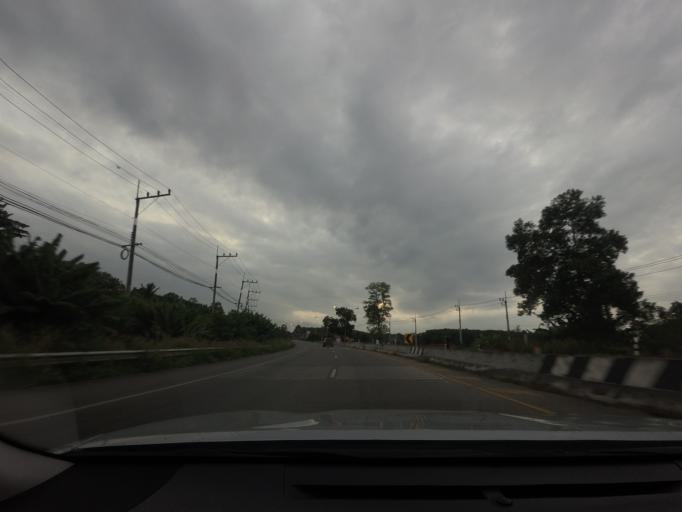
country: TH
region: Surat Thani
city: Khiri Ratthanikhom
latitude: 9.0426
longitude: 99.0848
